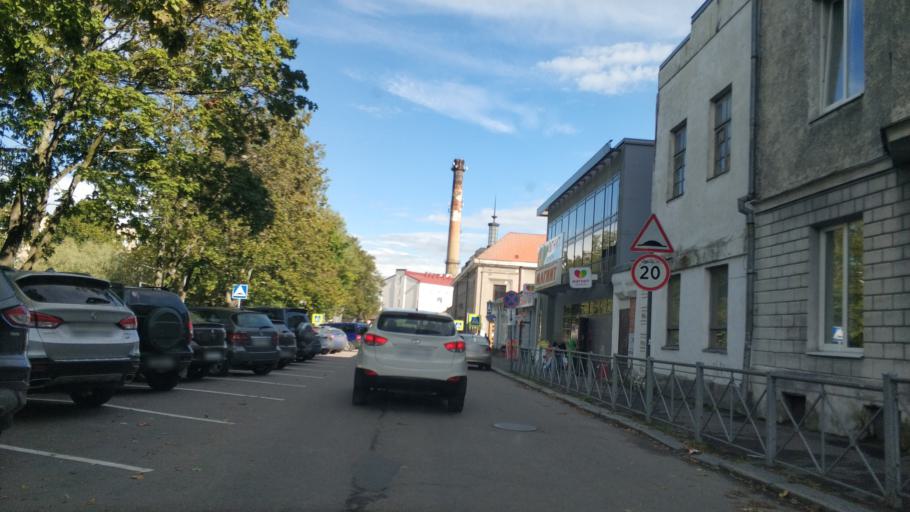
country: RU
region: Republic of Karelia
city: Sortavala
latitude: 61.7025
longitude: 30.6902
